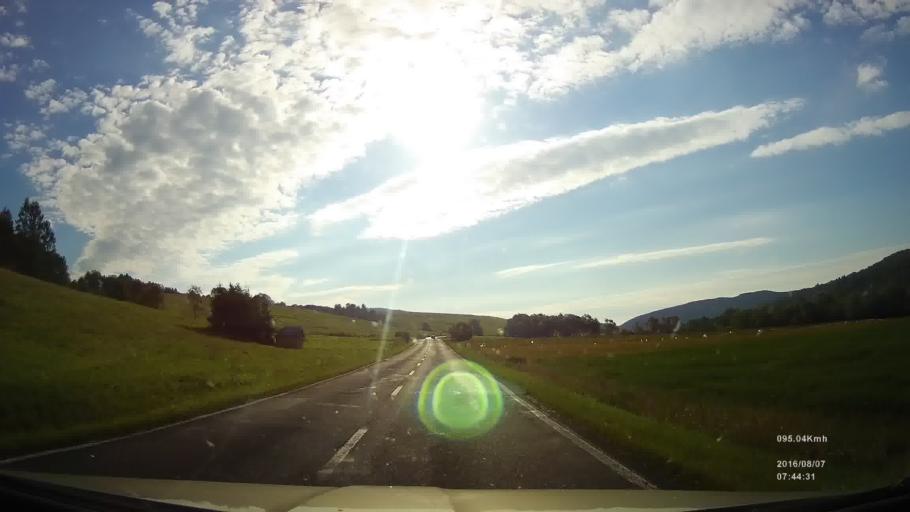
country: SK
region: Presovsky
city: Stropkov
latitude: 49.2651
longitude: 21.7264
